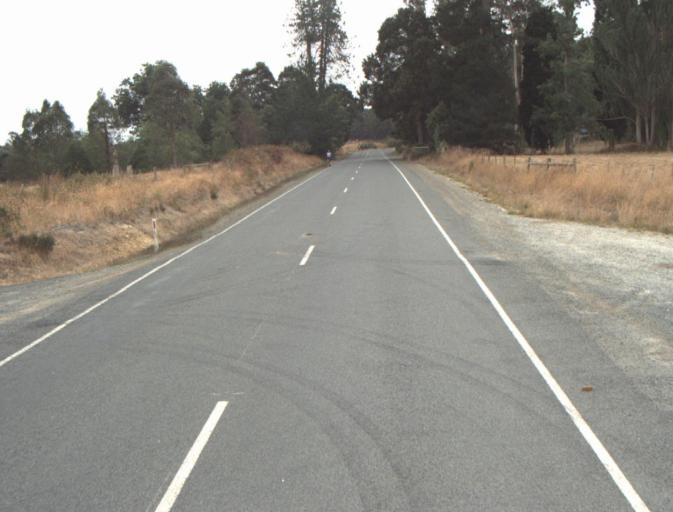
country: AU
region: Tasmania
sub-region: Launceston
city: Mayfield
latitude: -41.2317
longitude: 147.2101
